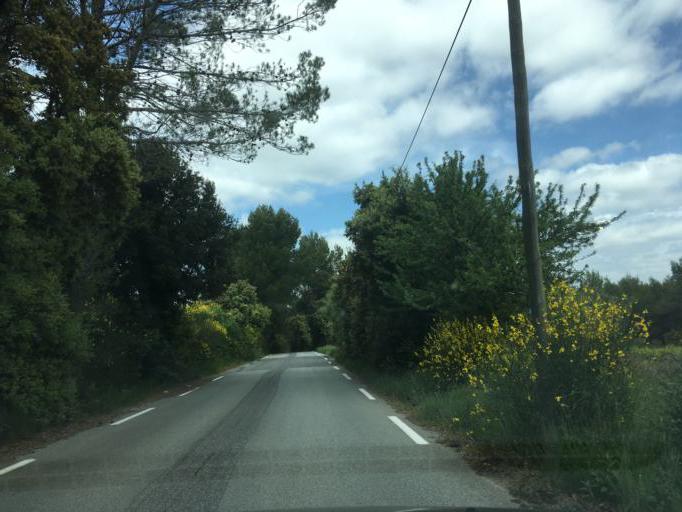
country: FR
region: Provence-Alpes-Cote d'Azur
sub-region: Departement du Var
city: Taradeau
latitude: 43.4635
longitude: 6.4324
